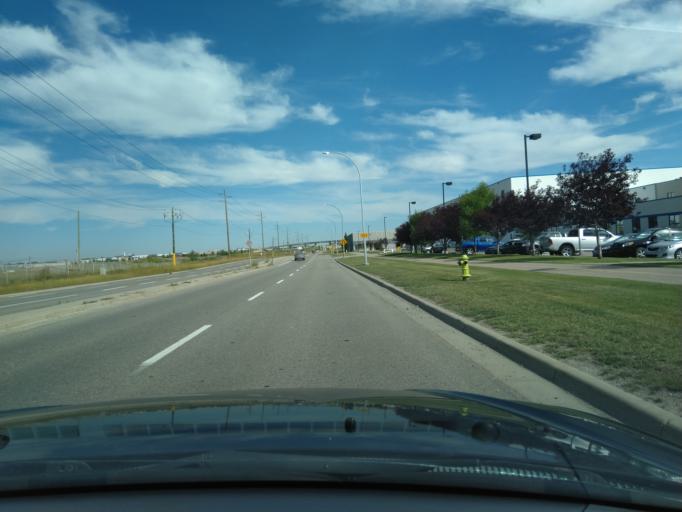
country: CA
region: Alberta
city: Calgary
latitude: 51.0959
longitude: -113.9982
